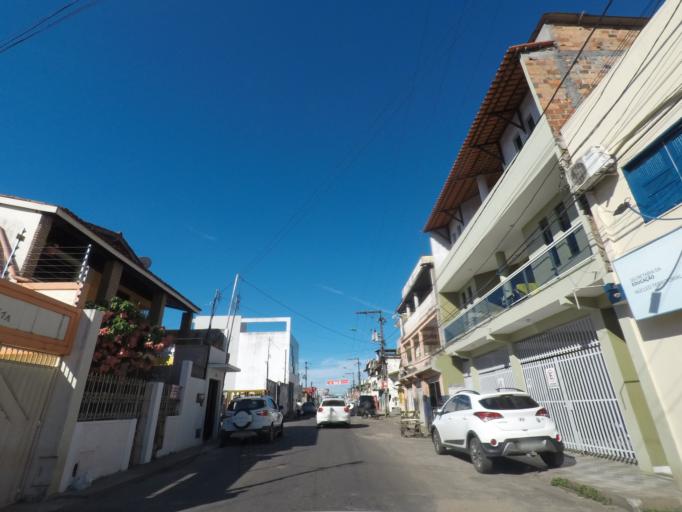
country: BR
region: Bahia
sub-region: Valenca
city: Valenca
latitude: -13.3680
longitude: -39.0701
